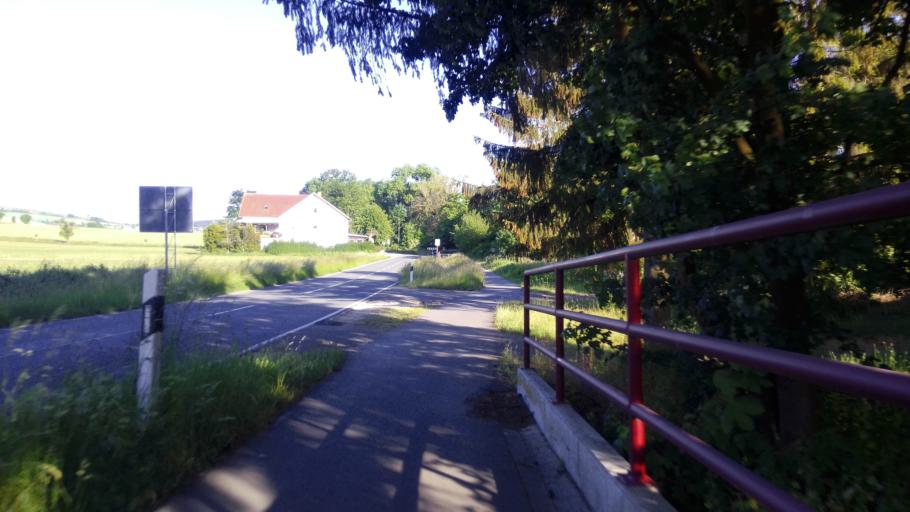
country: DE
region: Lower Saxony
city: Salzhemmendorf
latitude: 52.0374
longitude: 9.6054
